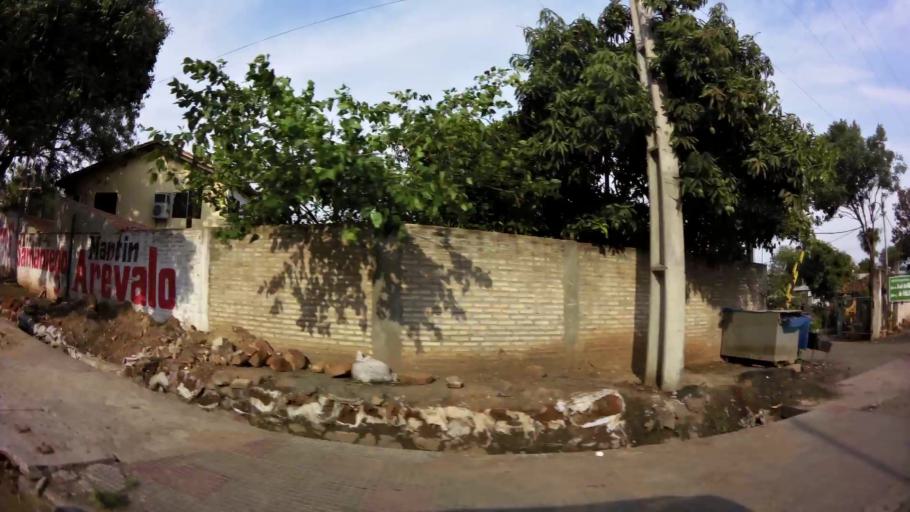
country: PY
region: Asuncion
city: Asuncion
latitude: -25.2741
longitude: -57.6099
